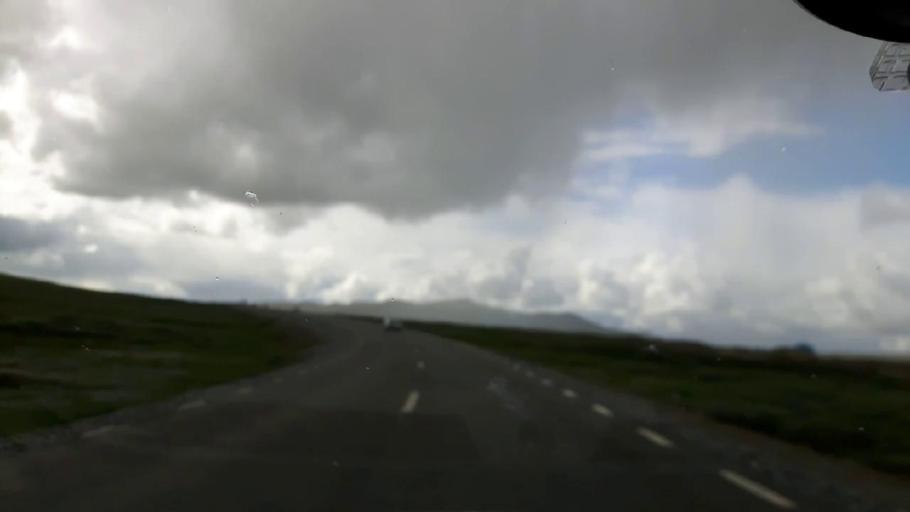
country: NO
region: Nordland
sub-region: Hattfjelldal
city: Hattfjelldal
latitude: 65.1026
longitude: 14.4687
